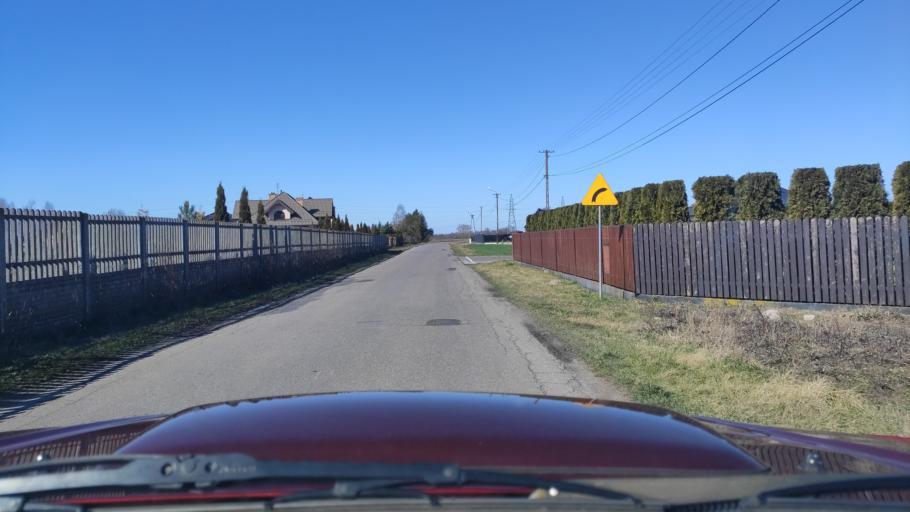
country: PL
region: Masovian Voivodeship
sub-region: Powiat zwolenski
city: Zwolen
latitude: 51.3726
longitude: 21.5858
